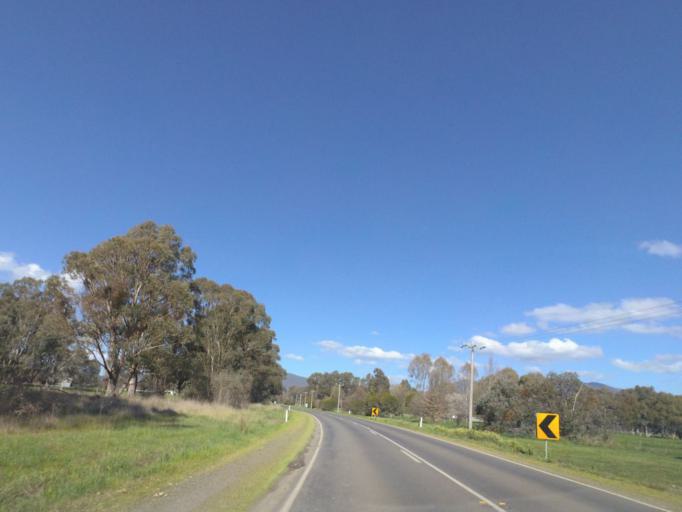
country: AU
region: Victoria
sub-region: Murrindindi
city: Alexandra
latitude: -37.2512
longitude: 145.7851
